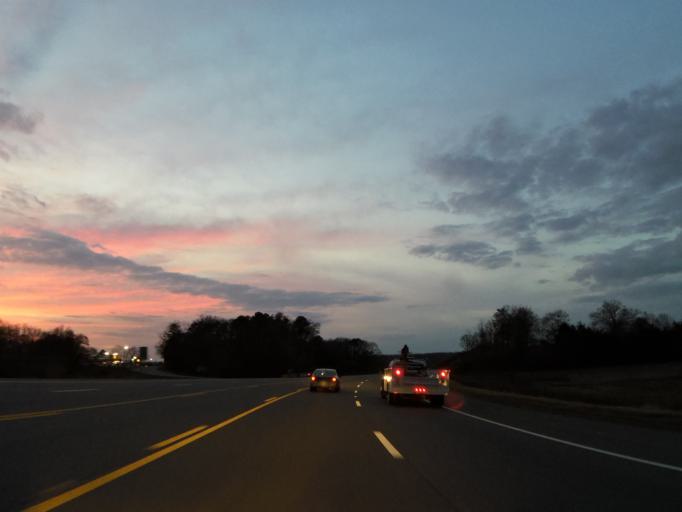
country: US
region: Tennessee
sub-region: Polk County
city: Benton
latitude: 35.1671
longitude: -84.6651
